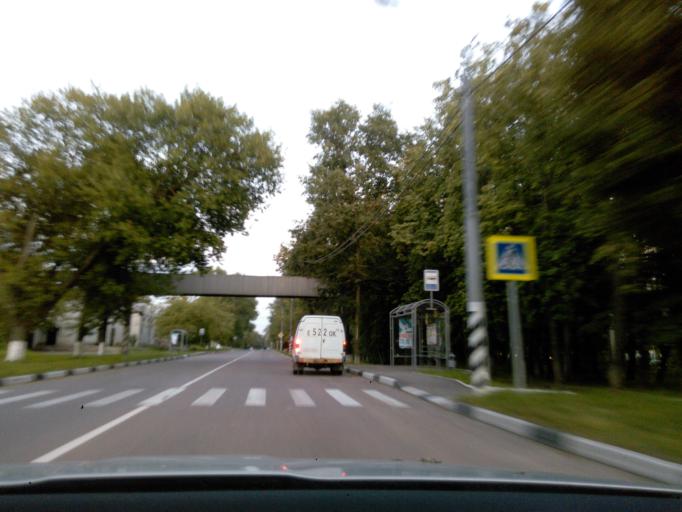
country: RU
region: Moskovskaya
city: Klin
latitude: 56.3401
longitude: 36.7154
